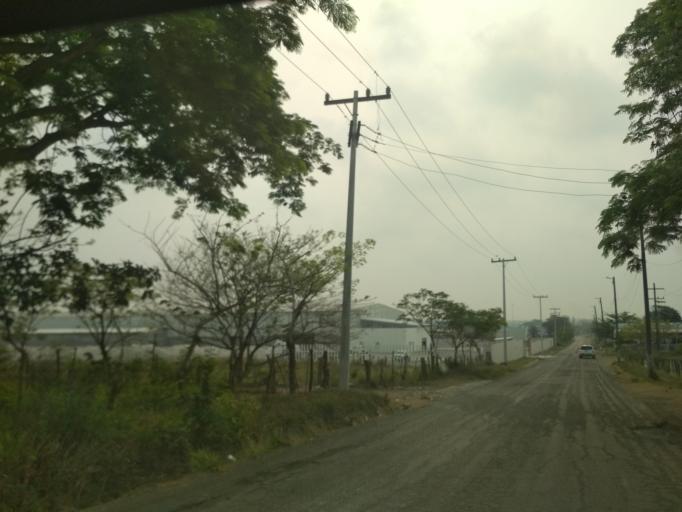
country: MX
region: Veracruz
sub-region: Veracruz
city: Delfino Victoria (Santa Fe)
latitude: 19.2098
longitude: -96.2564
